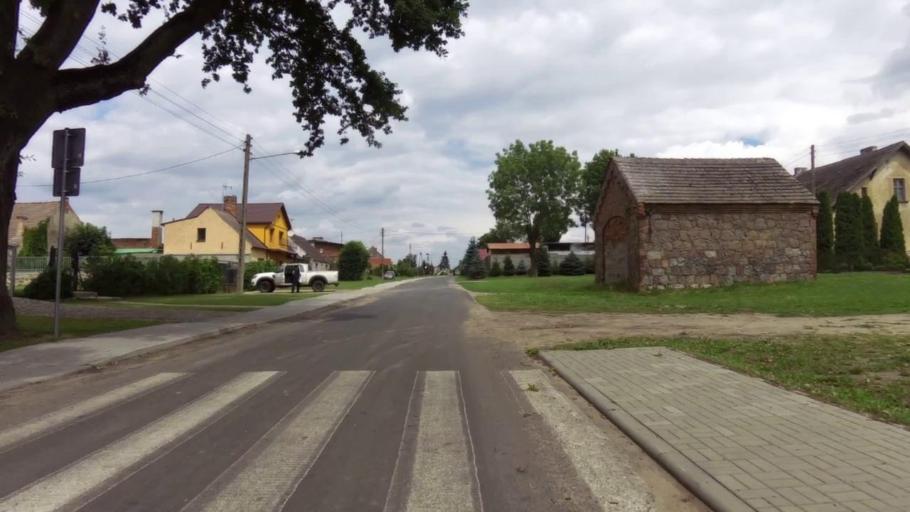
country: PL
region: West Pomeranian Voivodeship
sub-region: Powiat gryfinski
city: Moryn
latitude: 52.8730
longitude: 14.3355
